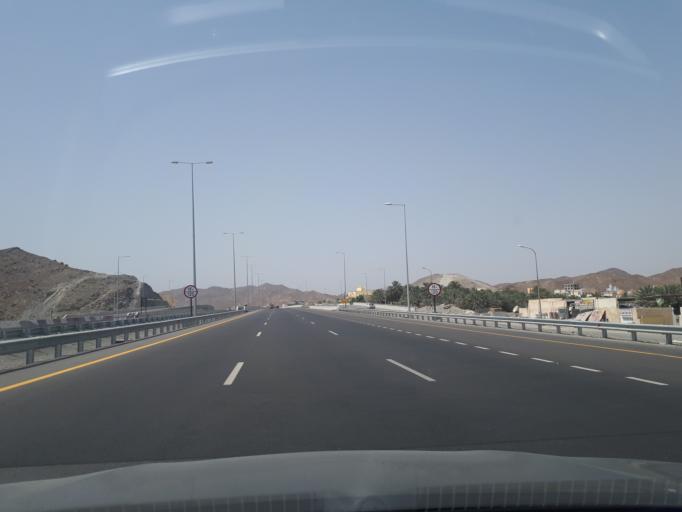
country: OM
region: Muhafazat ad Dakhiliyah
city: Bidbid
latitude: 23.4097
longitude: 58.1006
